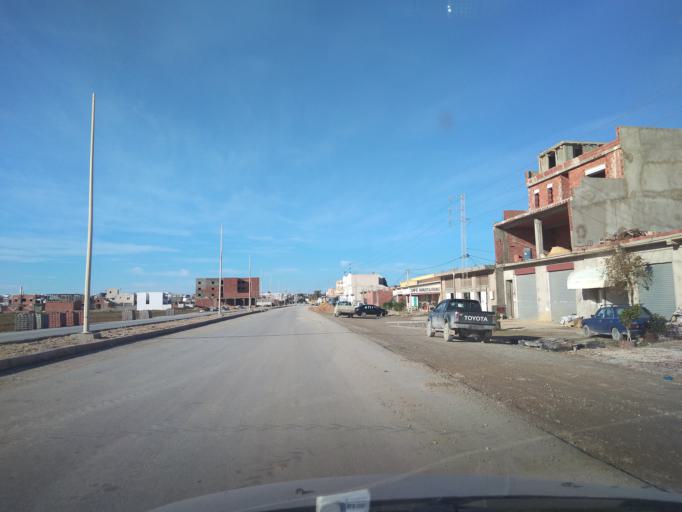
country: TN
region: Ariana
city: Qal'at al Andalus
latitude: 37.0496
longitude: 10.1238
